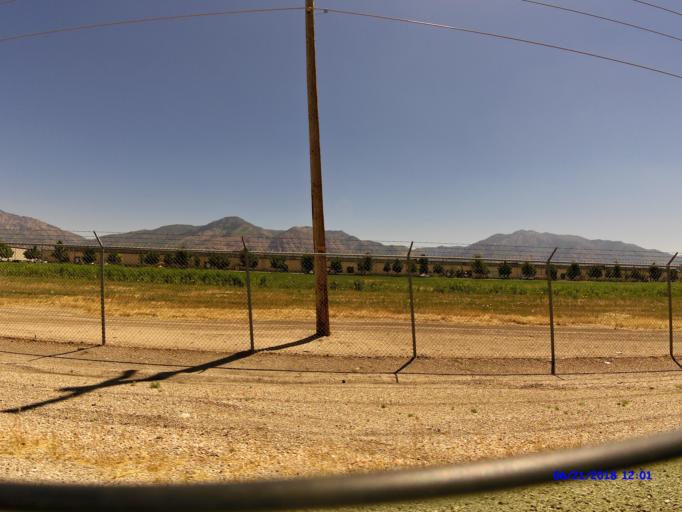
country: US
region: Utah
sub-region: Weber County
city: Marriott-Slaterville
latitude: 41.2611
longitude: -112.0091
